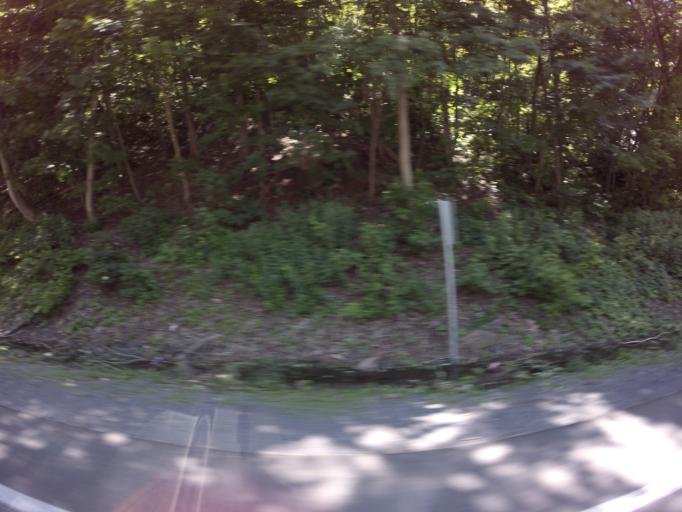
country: US
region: West Virginia
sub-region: Jefferson County
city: Bolivar
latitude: 39.3204
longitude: -77.7299
